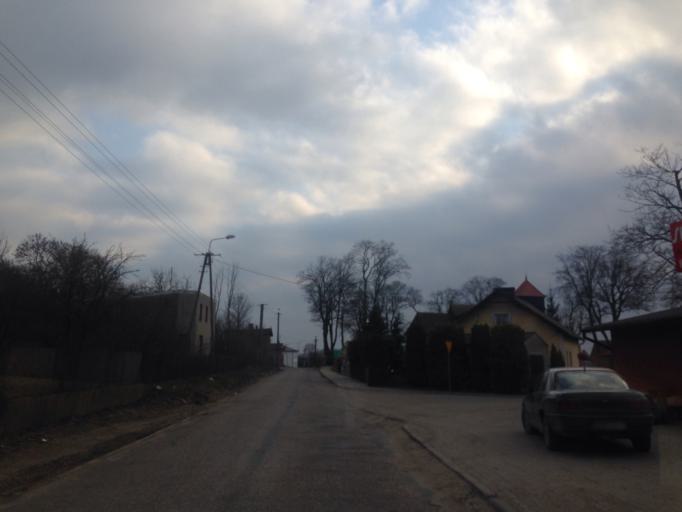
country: PL
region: Kujawsko-Pomorskie
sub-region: Powiat brodnicki
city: Brzozie
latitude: 53.3248
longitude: 19.7179
